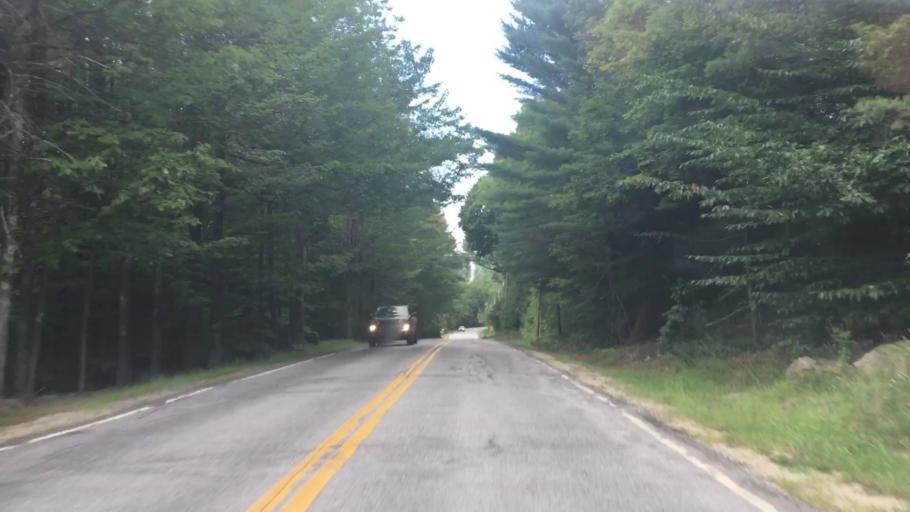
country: US
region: Maine
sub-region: Oxford County
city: Oxford
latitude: 44.0744
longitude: -70.5469
